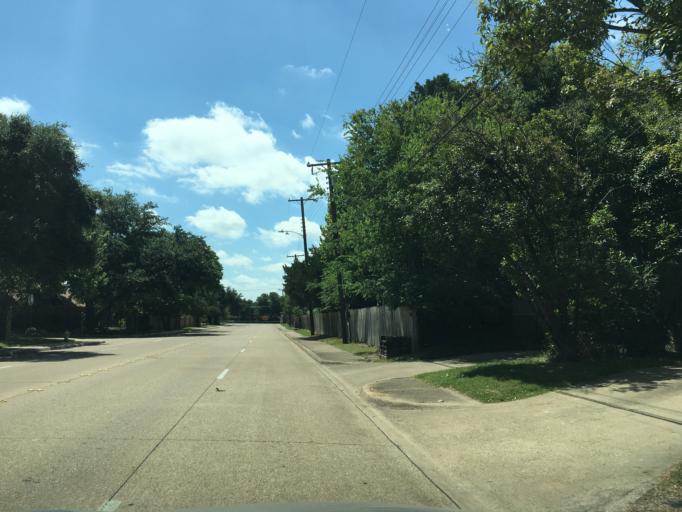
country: US
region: Texas
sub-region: Dallas County
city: Garland
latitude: 32.8383
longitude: -96.6490
